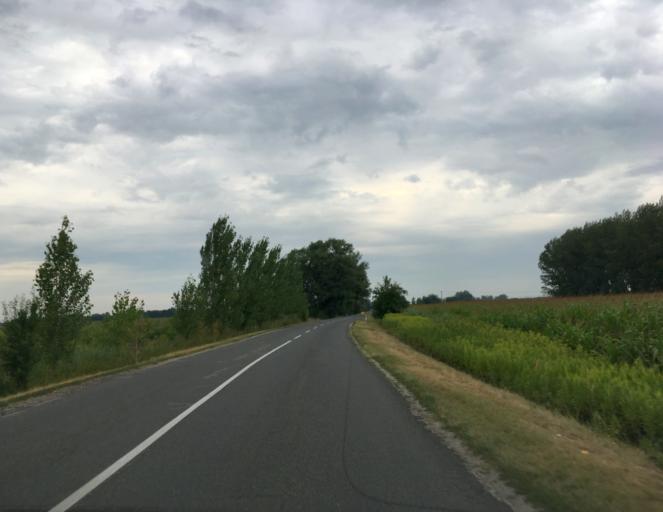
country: SK
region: Trnavsky
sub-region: Okres Dunajska Streda
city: Velky Meder
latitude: 47.8981
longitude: 17.6784
